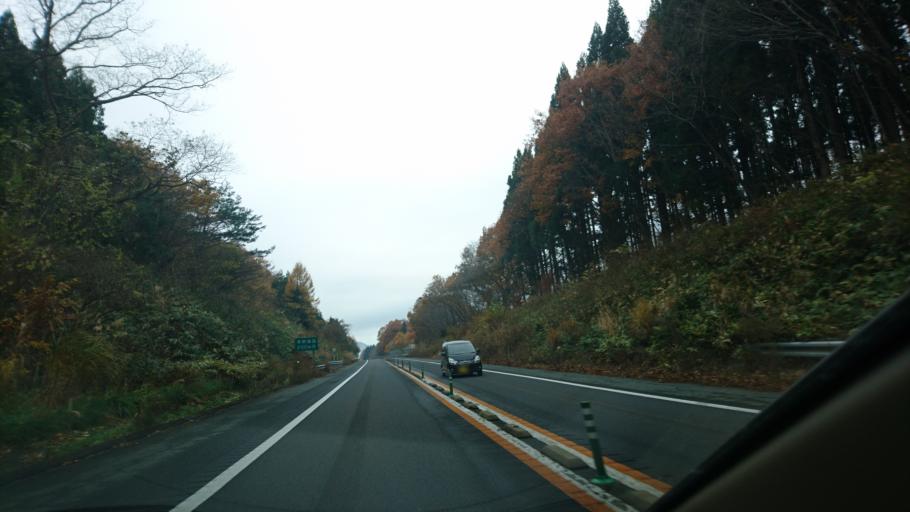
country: JP
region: Iwate
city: Kitakami
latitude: 39.2803
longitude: 141.0349
